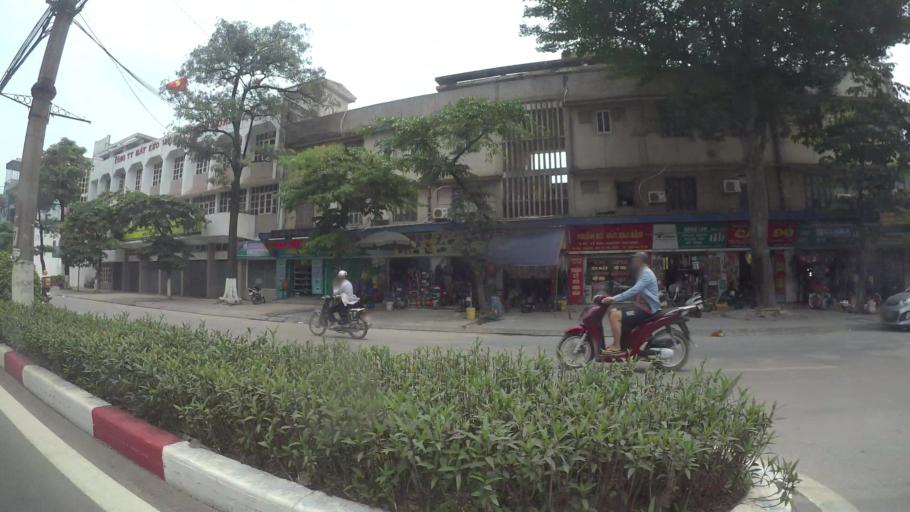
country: VN
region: Ha Noi
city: Ha Dong
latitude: 20.9748
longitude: 105.7776
